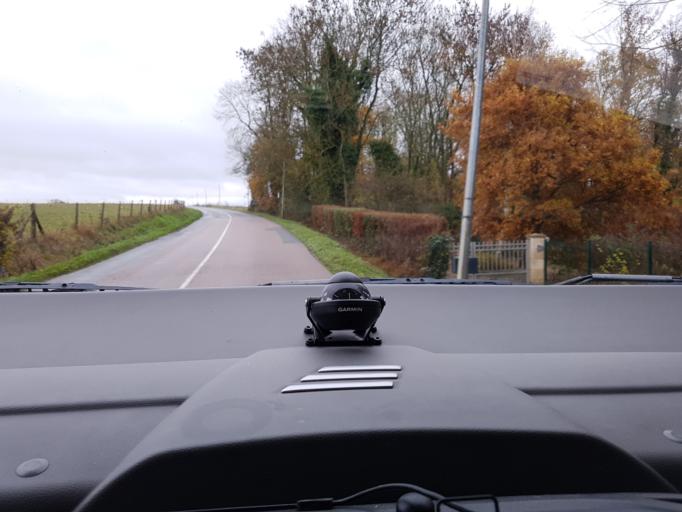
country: FR
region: Haute-Normandie
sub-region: Departement de l'Eure
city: Pont-Saint-Pierre
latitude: 49.3116
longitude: 1.3109
